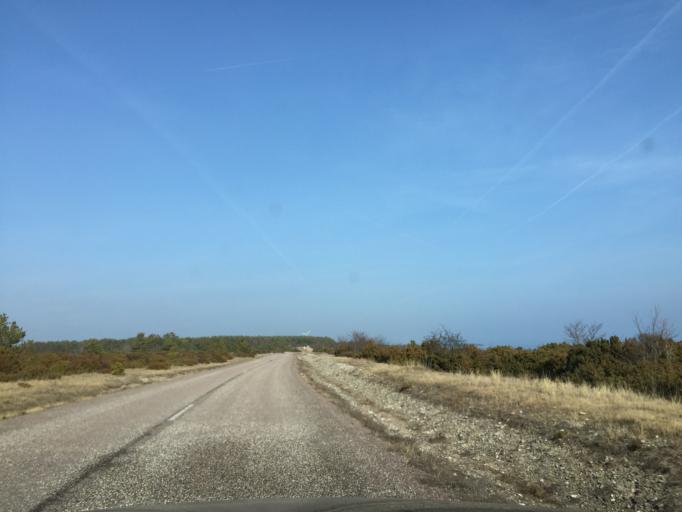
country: LV
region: Dundaga
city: Dundaga
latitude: 57.9147
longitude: 22.0598
